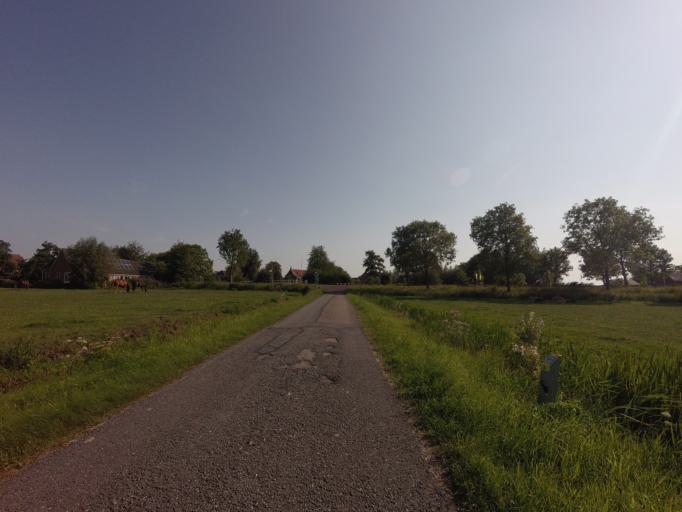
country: NL
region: Groningen
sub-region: Gemeente Zuidhorn
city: Zuidhorn
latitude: 53.2113
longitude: 6.4343
